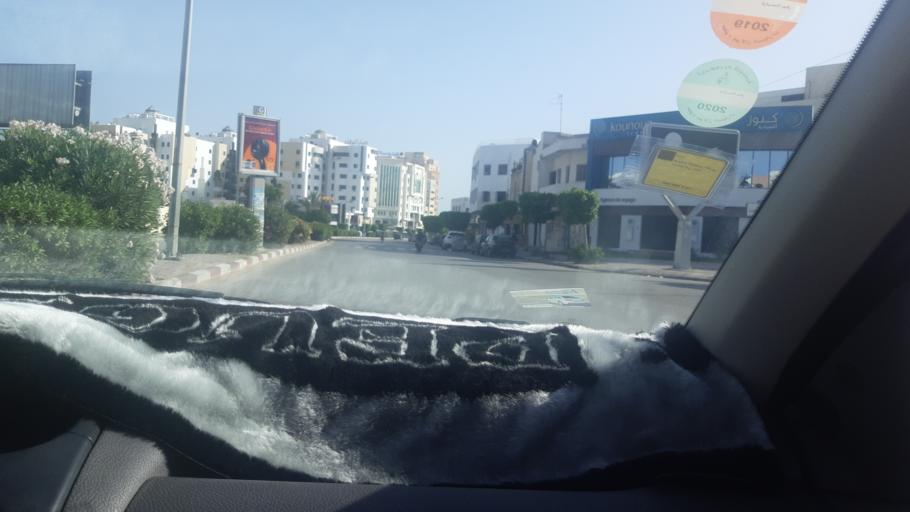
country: TN
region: Safaqis
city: Sfax
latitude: 34.7403
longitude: 10.7503
